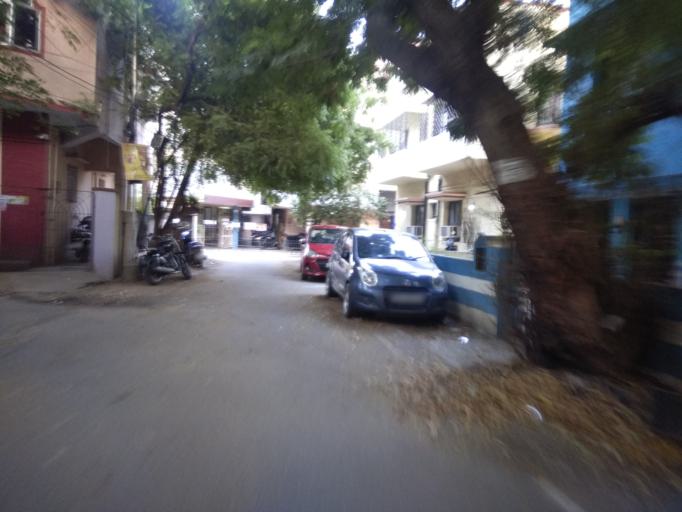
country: IN
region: Tamil Nadu
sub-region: Chennai
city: Chetput
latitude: 13.0713
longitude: 80.2093
